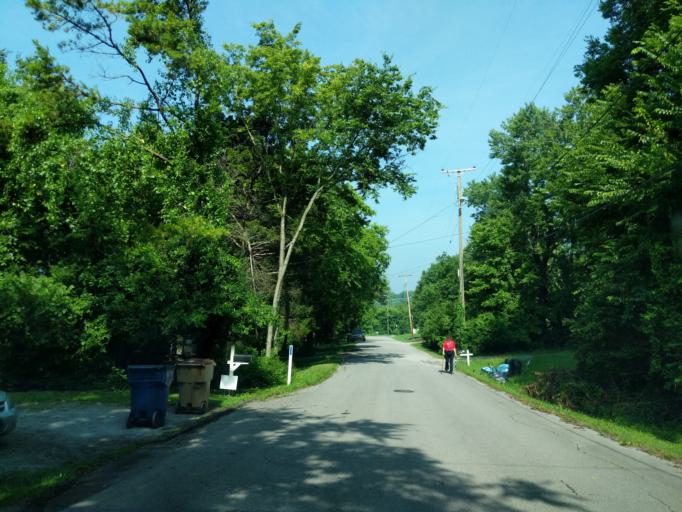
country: US
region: Tennessee
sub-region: Davidson County
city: Goodlettsville
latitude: 36.3083
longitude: -86.7011
